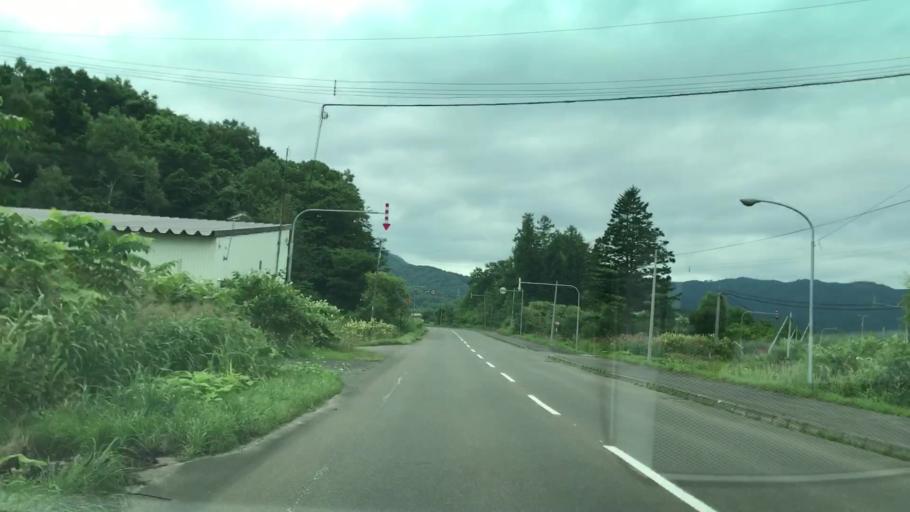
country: JP
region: Hokkaido
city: Yoichi
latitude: 43.0545
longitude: 140.8203
